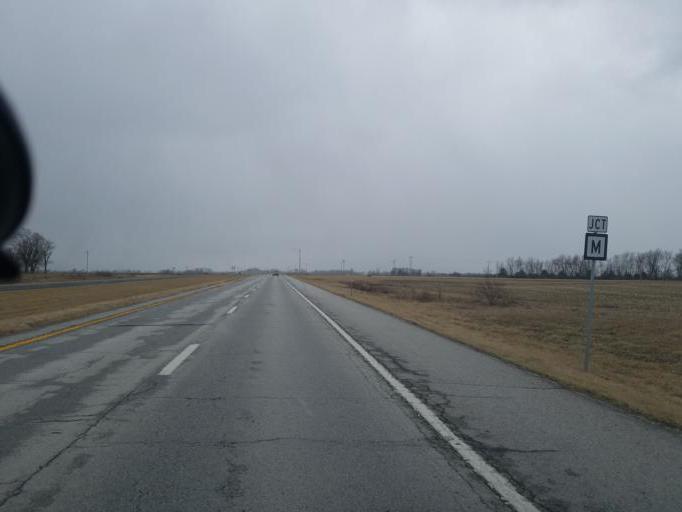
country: US
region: Missouri
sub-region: Macon County
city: La Plata
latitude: 39.8849
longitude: -92.4724
